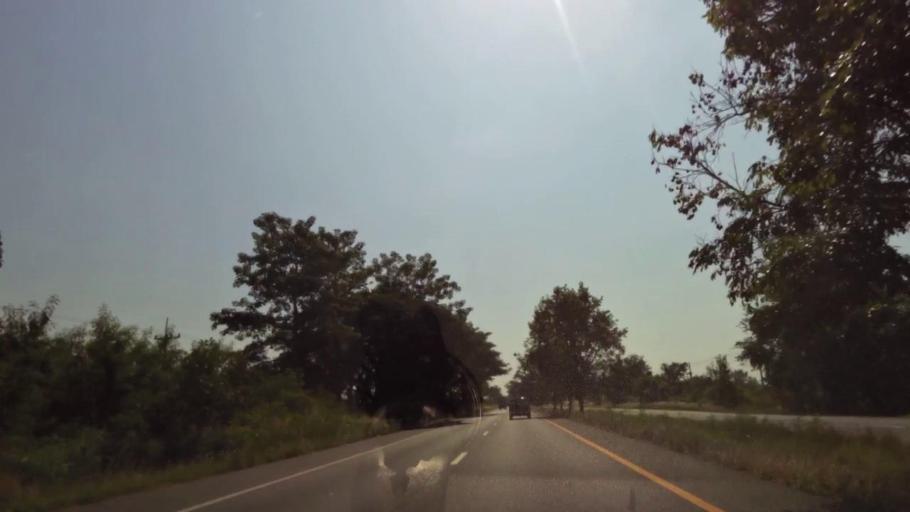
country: TH
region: Nakhon Sawan
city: Kao Liao
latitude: 15.9462
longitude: 100.1148
